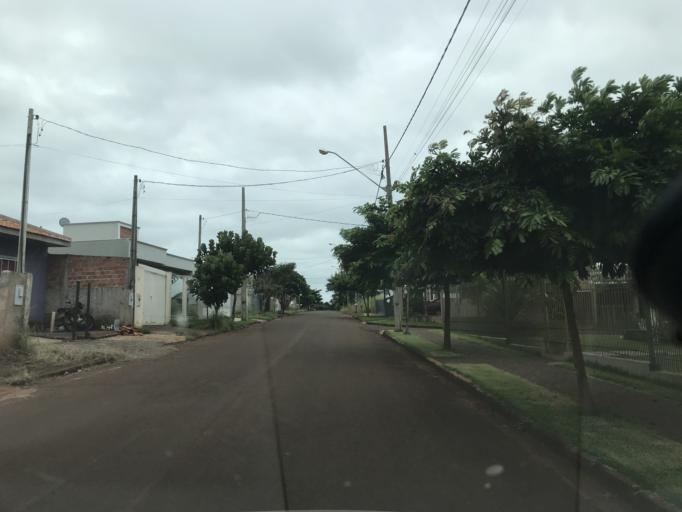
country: BR
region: Parana
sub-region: Palotina
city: Palotina
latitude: -24.2974
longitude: -53.8285
